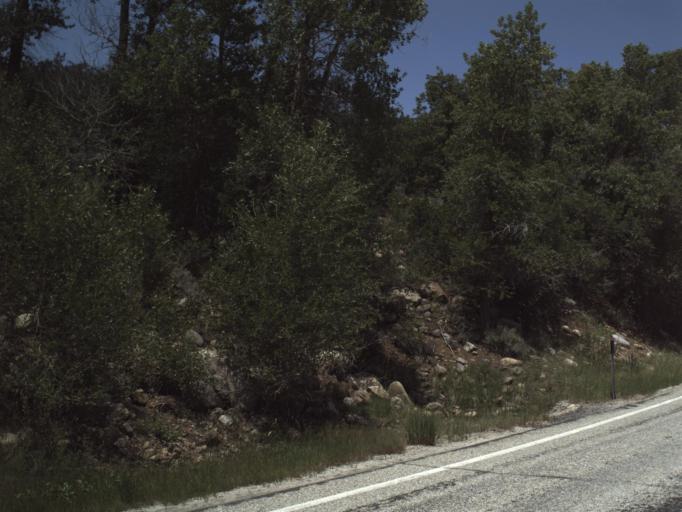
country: US
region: Utah
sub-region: Weber County
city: Wolf Creek
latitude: 41.3311
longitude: -111.6117
